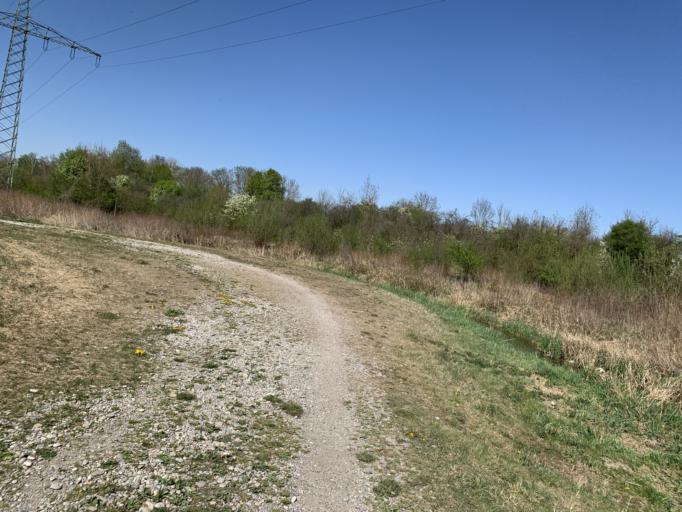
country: DE
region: Bavaria
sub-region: Swabia
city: Gersthofen
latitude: 48.4351
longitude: 10.8922
